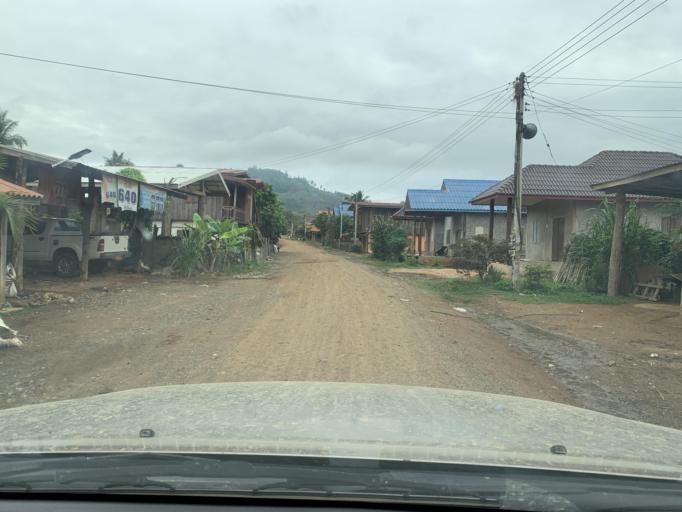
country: TH
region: Nan
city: Mae Charim
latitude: 18.4201
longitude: 101.4487
